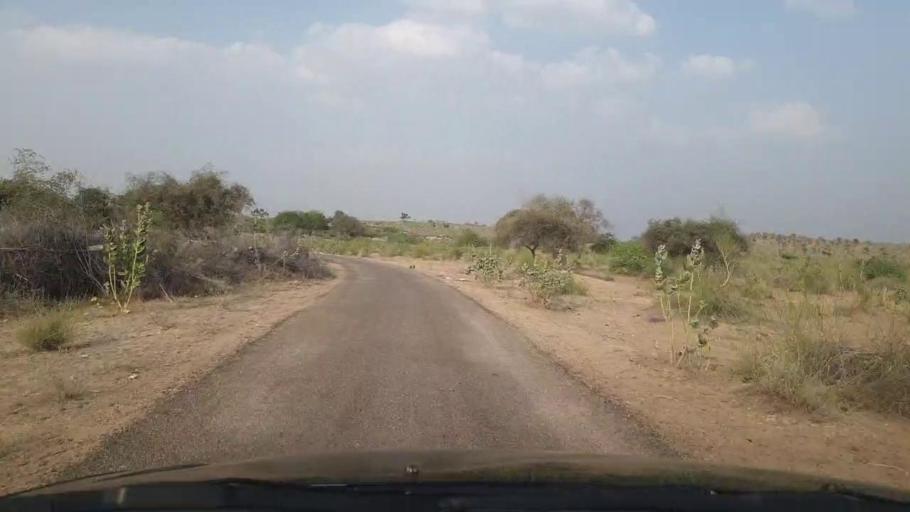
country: PK
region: Sindh
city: Islamkot
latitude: 25.0658
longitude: 70.5654
